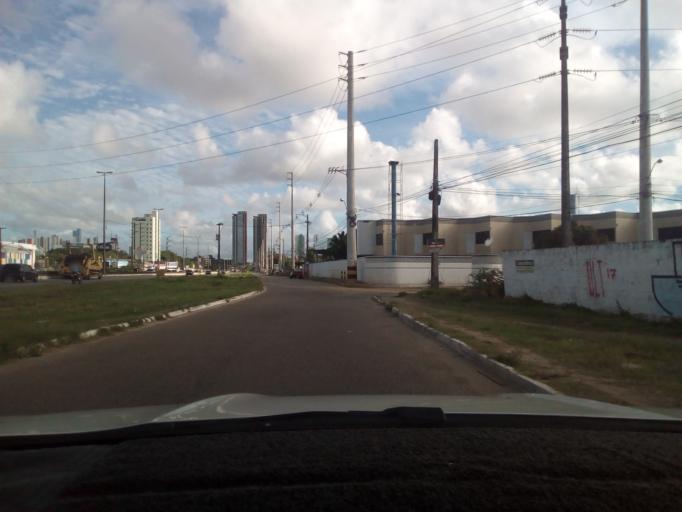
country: BR
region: Paraiba
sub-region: Joao Pessoa
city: Joao Pessoa
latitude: -7.0910
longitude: -34.8485
